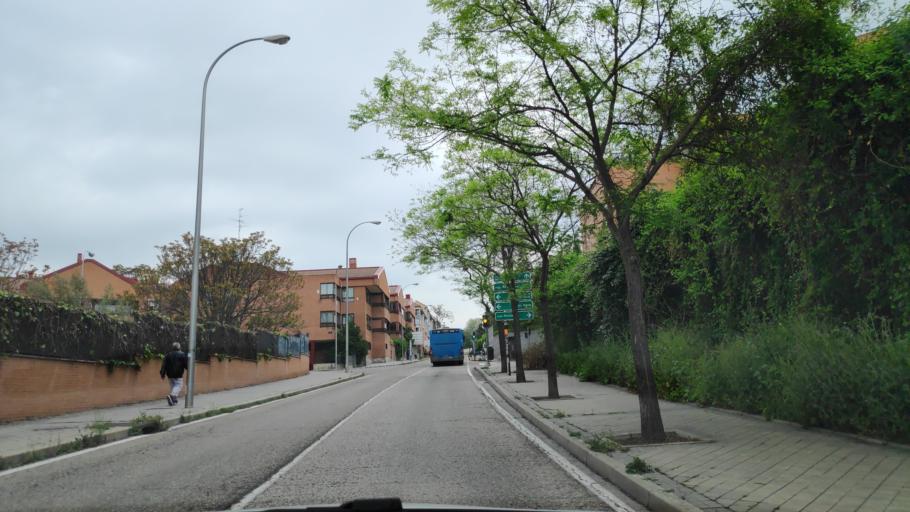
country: ES
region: Madrid
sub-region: Provincia de Madrid
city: Pozuelo de Alarcon
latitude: 40.4559
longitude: -3.7809
